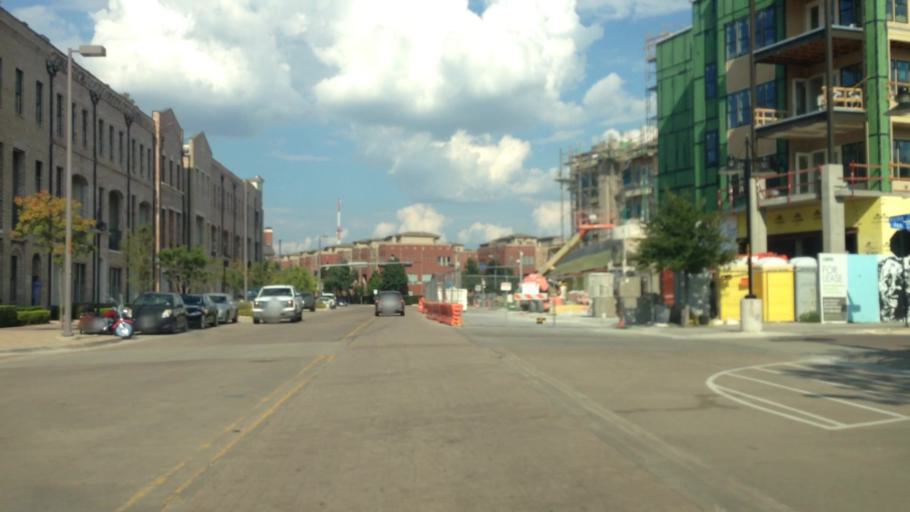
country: US
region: Texas
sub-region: Dallas County
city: Dallas
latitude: 32.7782
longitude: -96.7901
